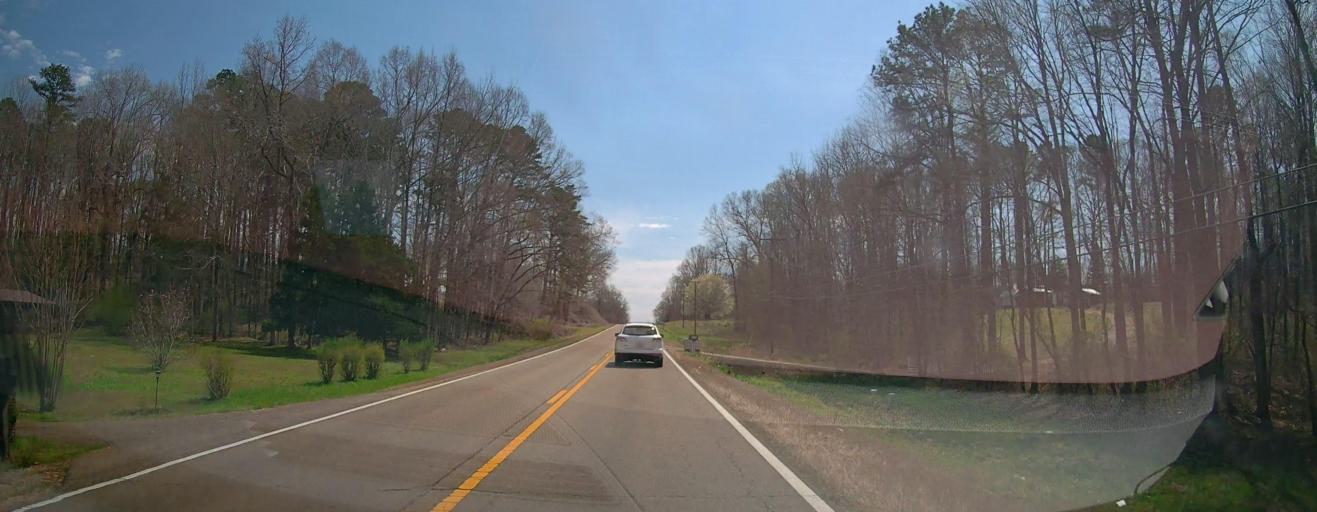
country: US
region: Mississippi
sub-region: Union County
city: New Albany
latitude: 34.4427
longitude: -88.9632
